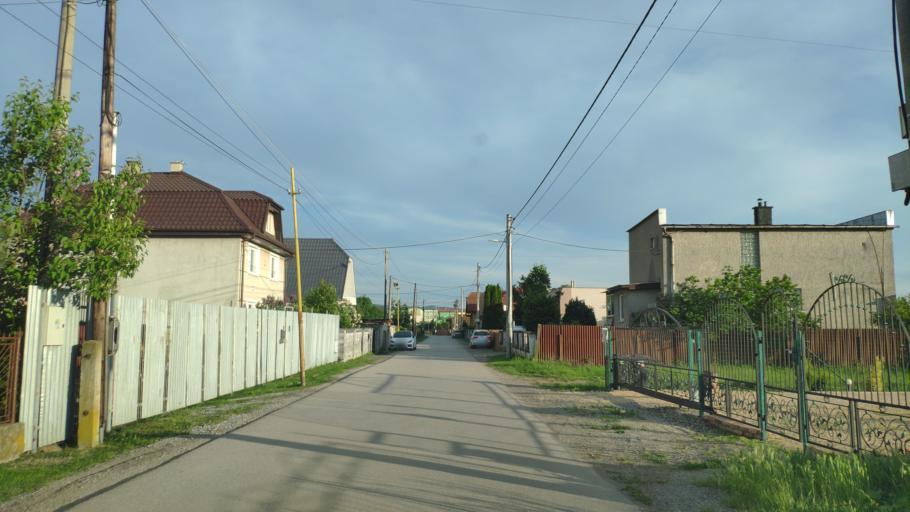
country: SK
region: Kosicky
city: Kosice
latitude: 48.6164
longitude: 21.3235
